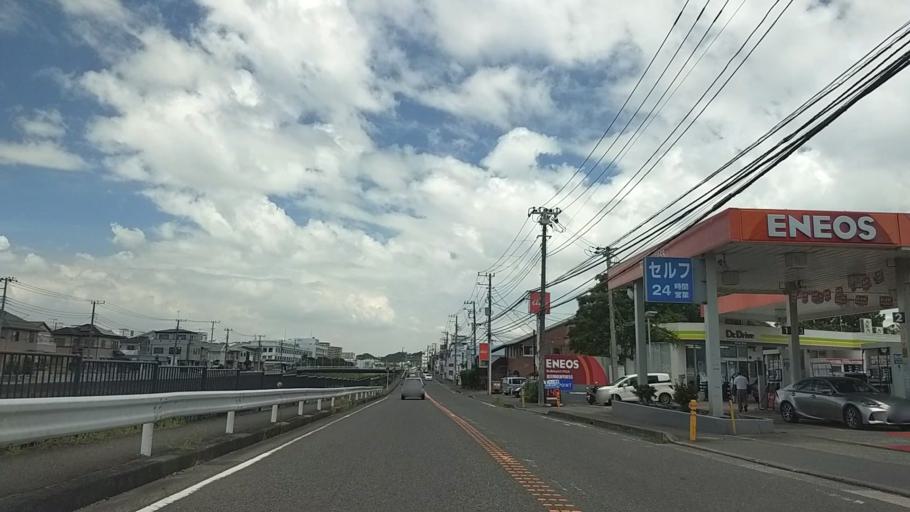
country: JP
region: Kanagawa
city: Fujisawa
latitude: 35.3339
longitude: 139.5105
